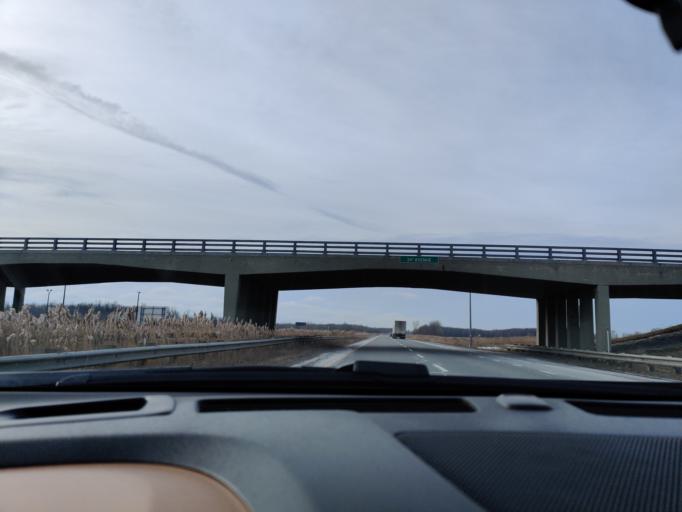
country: CA
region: Quebec
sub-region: Monteregie
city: Les Coteaux
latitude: 45.2527
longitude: -74.2540
